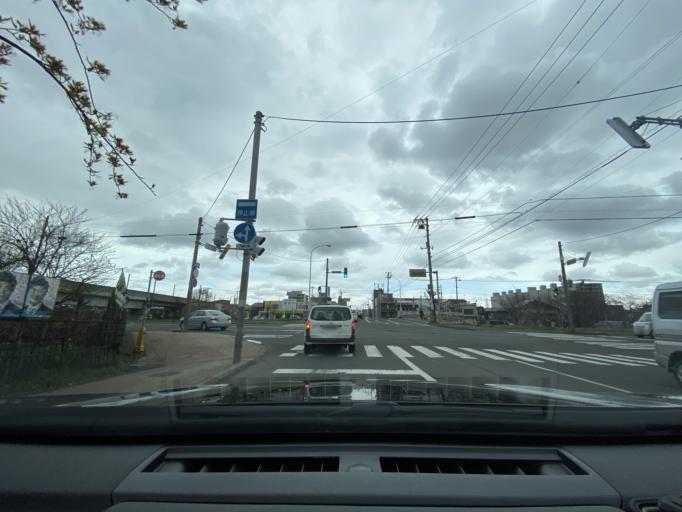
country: JP
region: Hokkaido
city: Sapporo
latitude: 43.0920
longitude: 141.3197
